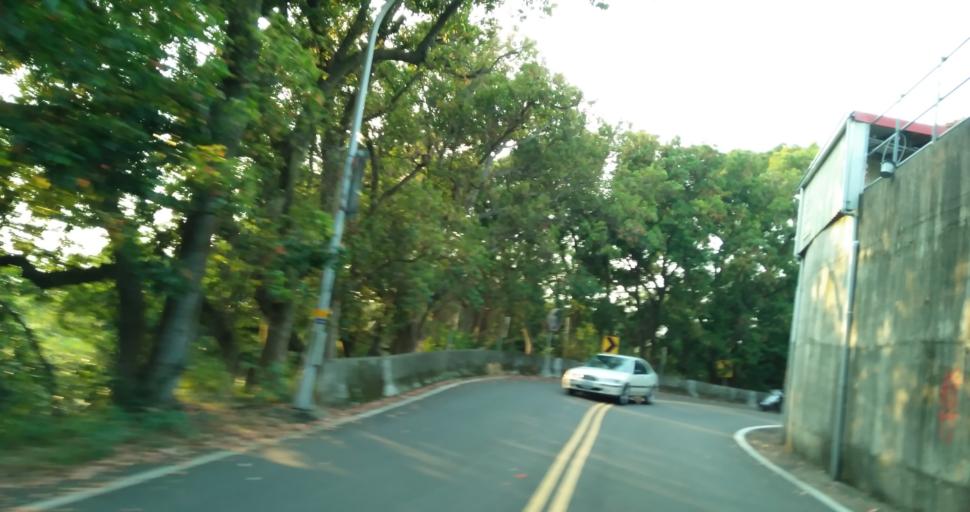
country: TW
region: Taiwan
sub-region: Hsinchu
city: Hsinchu
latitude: 24.7762
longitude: 120.9770
